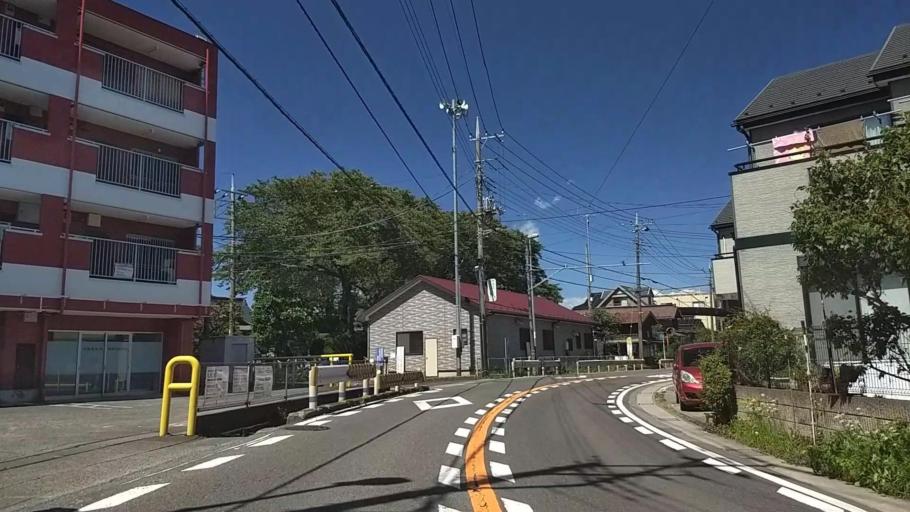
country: JP
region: Kanagawa
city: Zama
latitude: 35.5420
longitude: 139.3384
